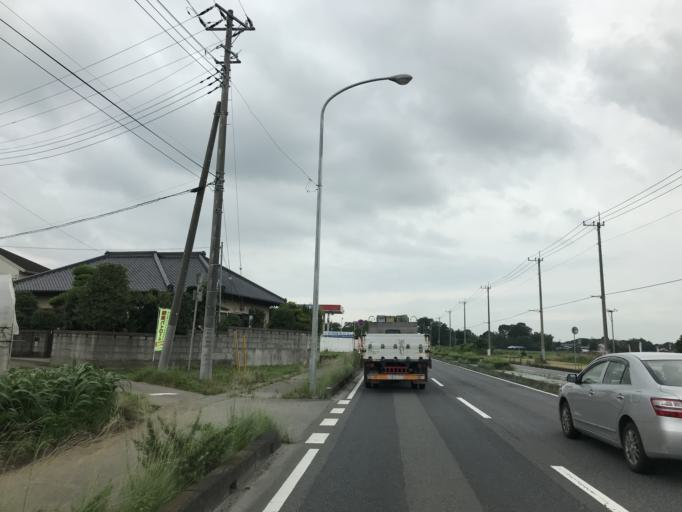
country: JP
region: Ibaraki
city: Naka
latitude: 36.1314
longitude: 140.1529
